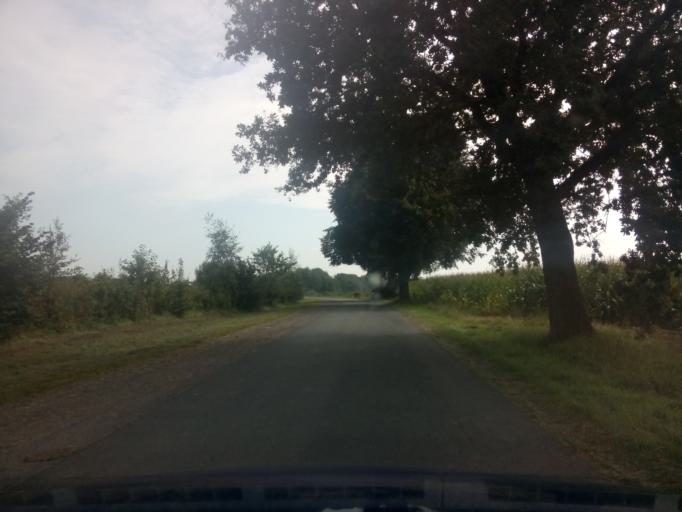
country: DE
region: Lower Saxony
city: Osterholz-Scharmbeck
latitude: 53.2492
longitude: 8.7566
